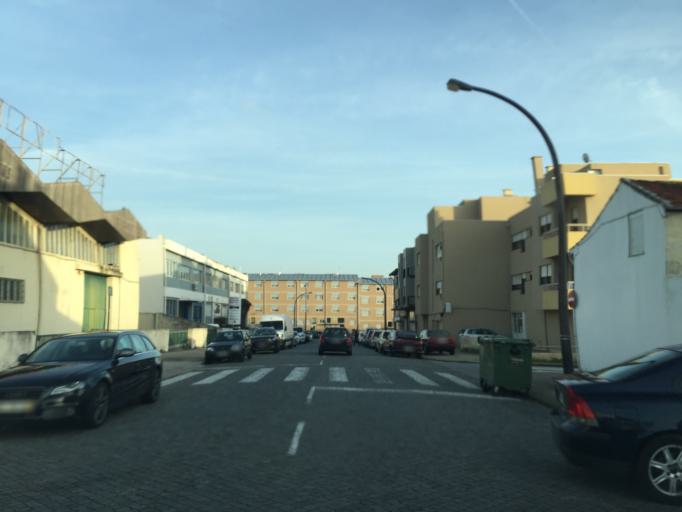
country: PT
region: Porto
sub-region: Matosinhos
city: Senhora da Hora
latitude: 41.1707
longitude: -8.6498
